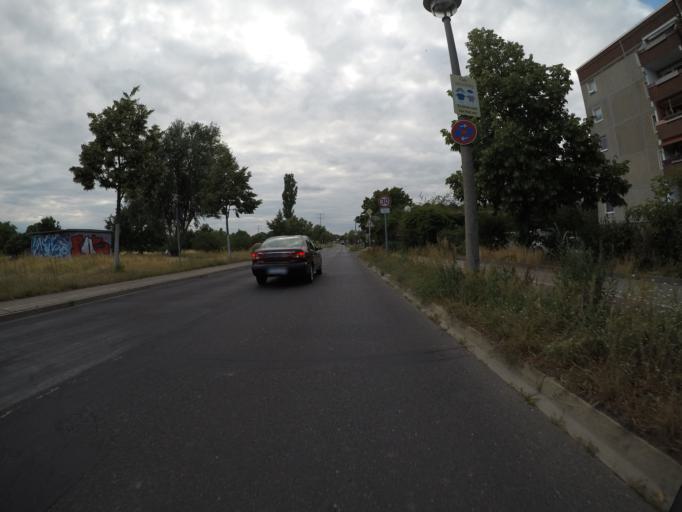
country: DE
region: Berlin
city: Kaulsdorf
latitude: 52.5188
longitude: 13.6020
